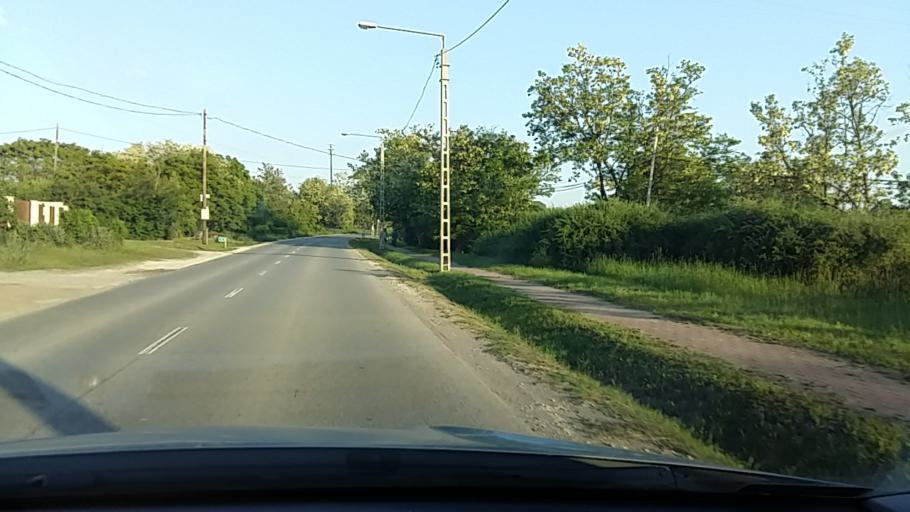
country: HU
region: Pest
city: Orbottyan
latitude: 47.6891
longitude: 19.2586
